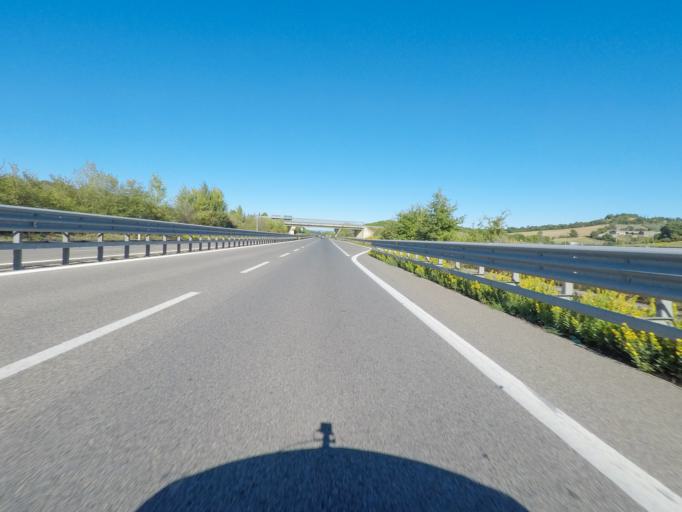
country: IT
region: Tuscany
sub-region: Provincia di Grosseto
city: Campagnatico
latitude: 42.8763
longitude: 11.2115
